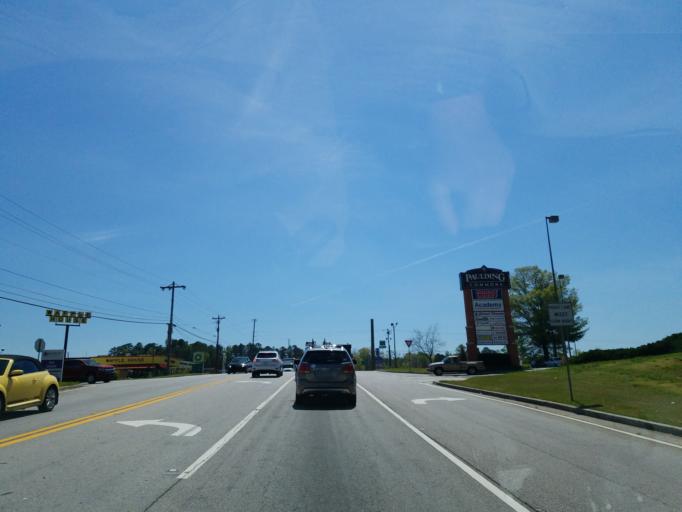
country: US
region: Georgia
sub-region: Paulding County
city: Hiram
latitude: 33.8931
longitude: -84.7542
